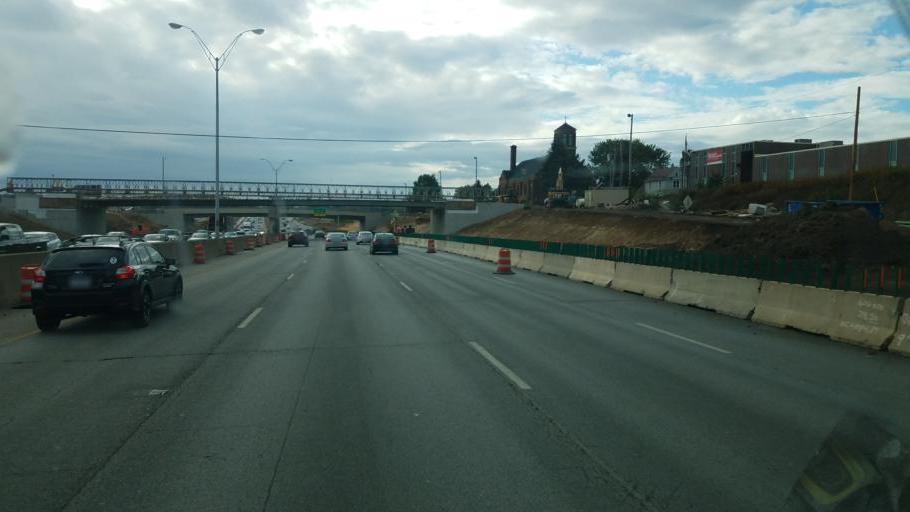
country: US
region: Ohio
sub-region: Summit County
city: Akron
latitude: 41.0627
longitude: -81.5165
